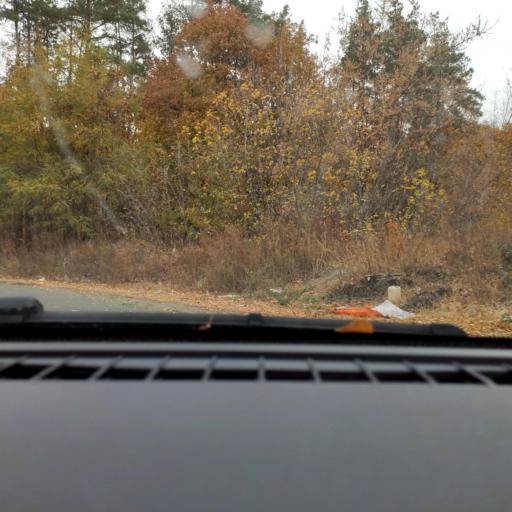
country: RU
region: Voronezj
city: Somovo
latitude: 51.6867
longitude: 39.3004
